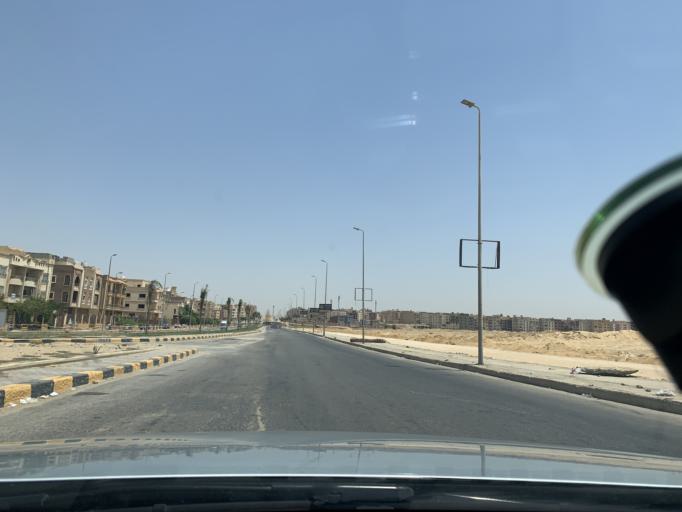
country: EG
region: Muhafazat al Qahirah
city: Cairo
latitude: 29.9993
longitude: 31.4635
